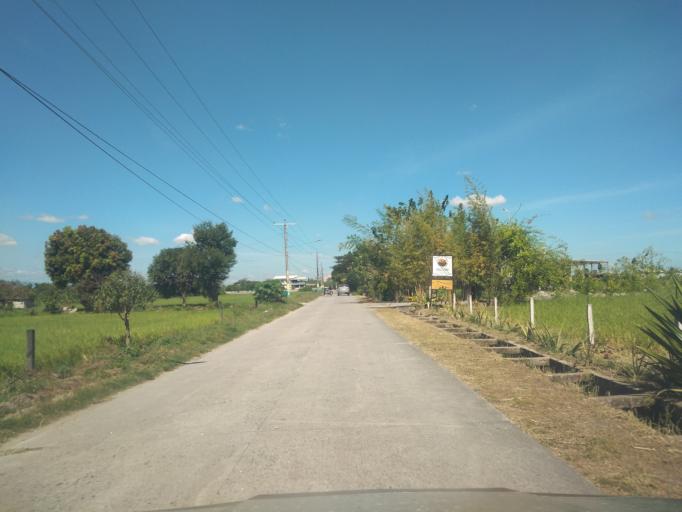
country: PH
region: Central Luzon
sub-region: Province of Pampanga
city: Bacolor
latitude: 15.0205
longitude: 120.6393
